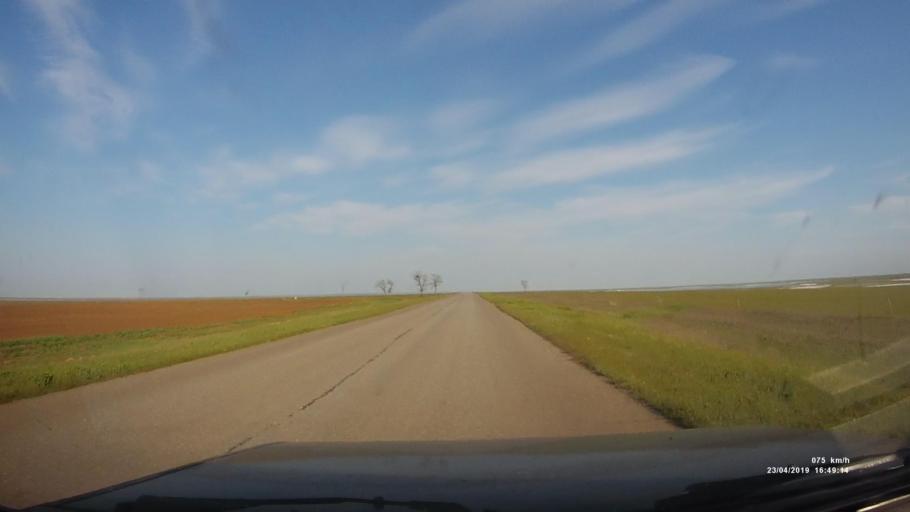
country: RU
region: Kalmykiya
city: Priyutnoye
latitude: 46.3319
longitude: 43.2733
